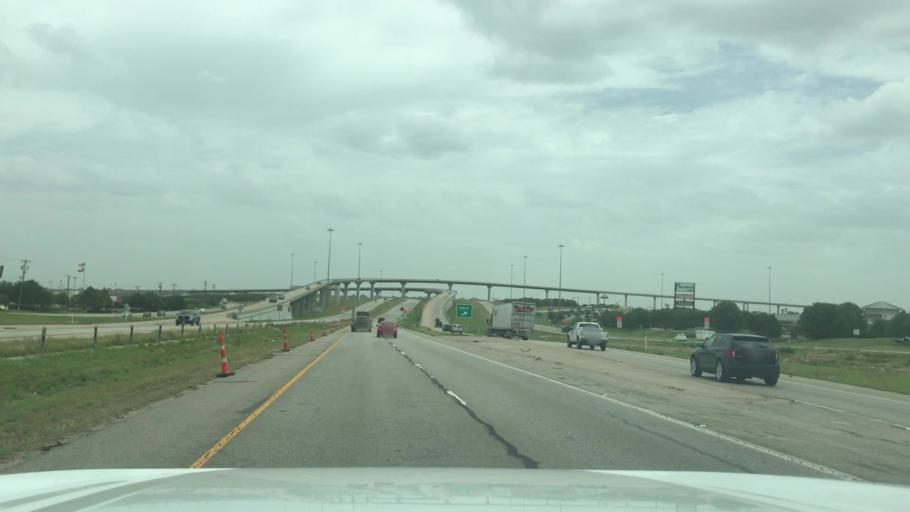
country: US
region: Texas
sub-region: McLennan County
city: Beverly Hills
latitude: 31.4967
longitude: -97.1597
